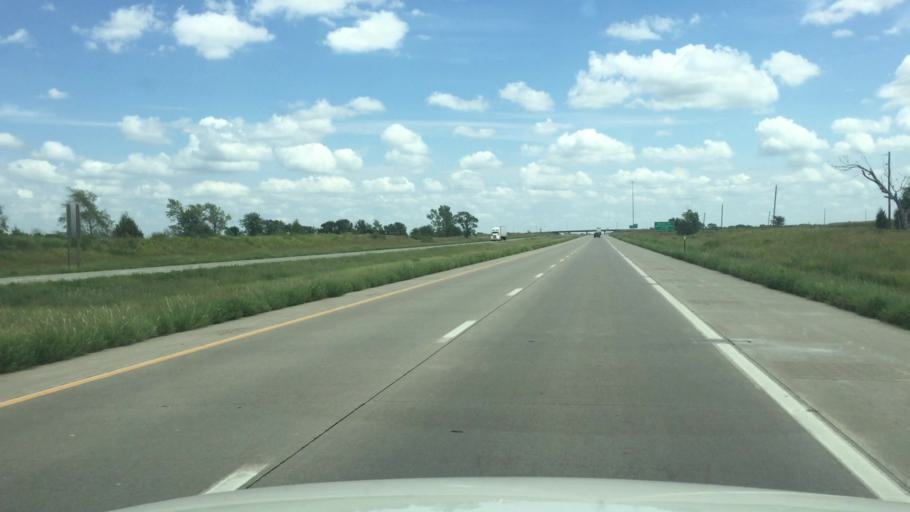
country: US
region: Kansas
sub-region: Franklin County
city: Wellsville
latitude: 38.6658
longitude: -95.1673
